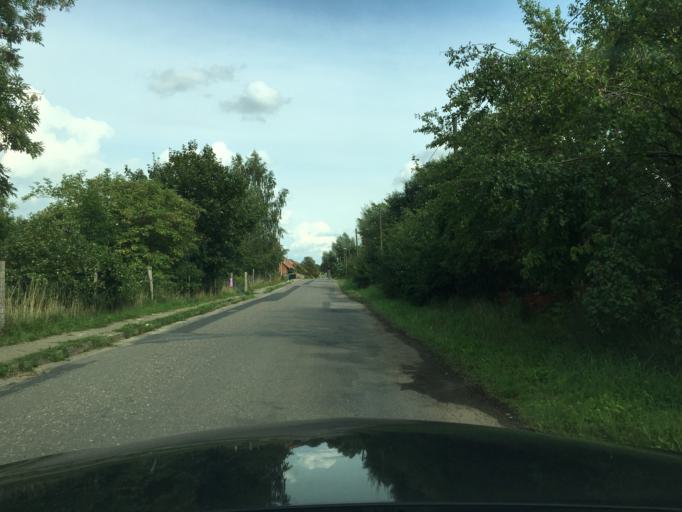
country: DE
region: Mecklenburg-Vorpommern
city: Mollenhagen
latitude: 53.5071
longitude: 12.8667
